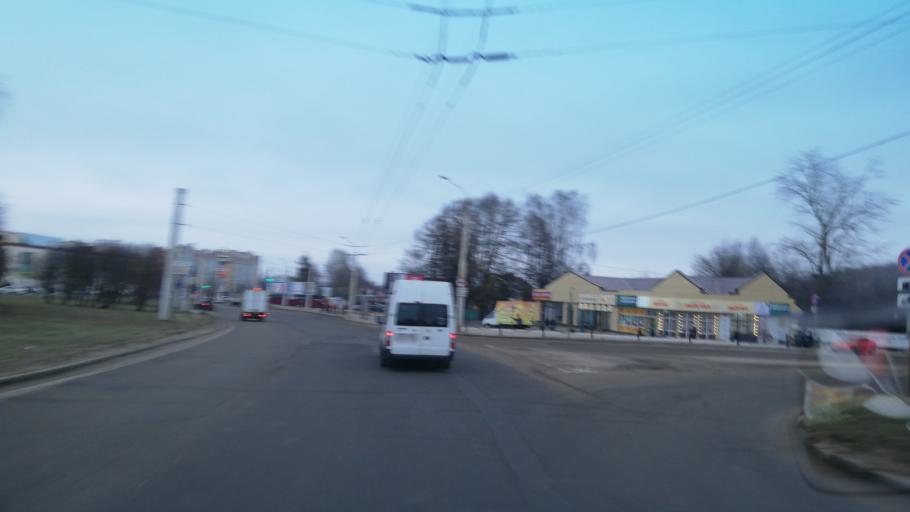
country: RU
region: Kostroma
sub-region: Kostromskoy Rayon
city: Kostroma
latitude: 57.7396
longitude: 40.9167
